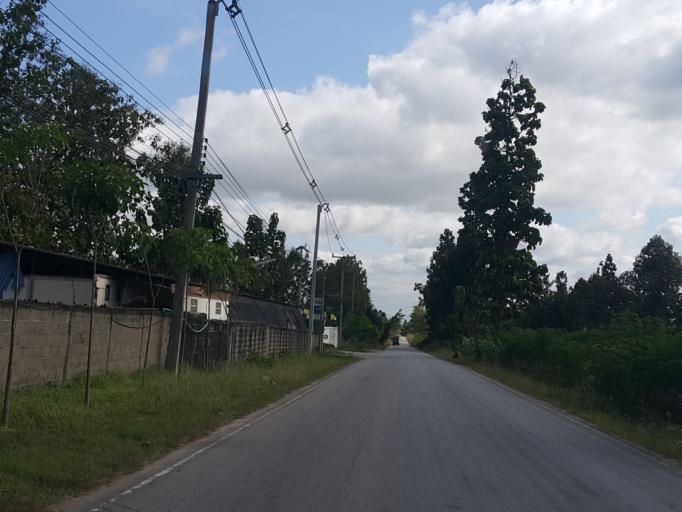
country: TH
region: Lampang
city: Hang Chat
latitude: 18.3424
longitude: 99.3778
